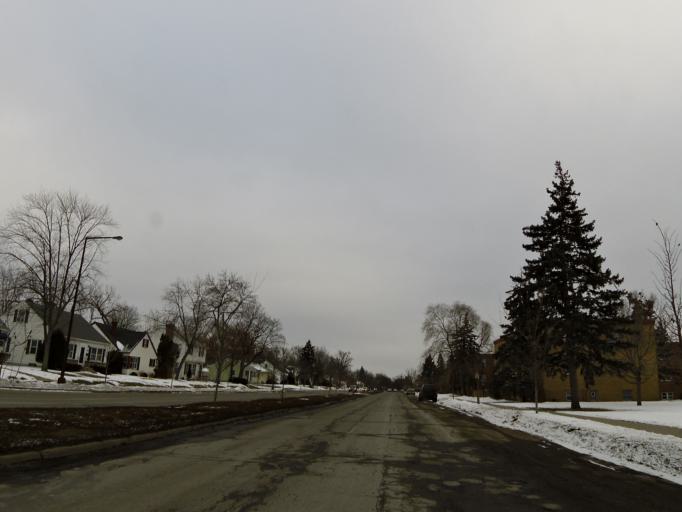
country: US
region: Minnesota
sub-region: Dakota County
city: Mendota Heights
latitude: 44.9156
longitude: -93.1871
